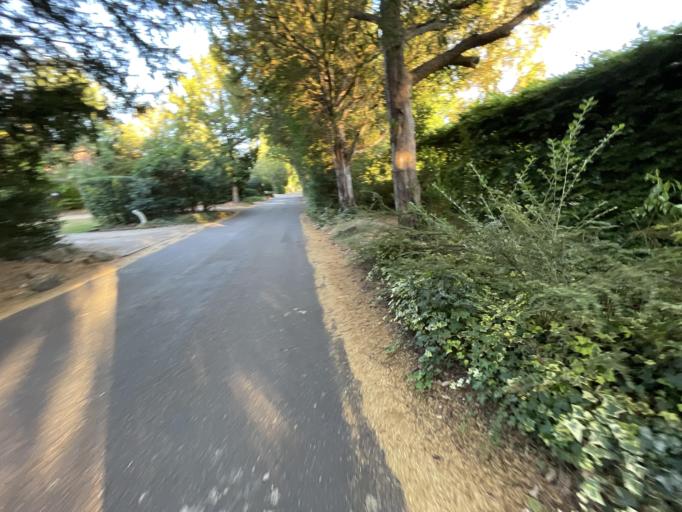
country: GB
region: England
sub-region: Surrey
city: East Horsley
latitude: 51.2725
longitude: -0.4299
